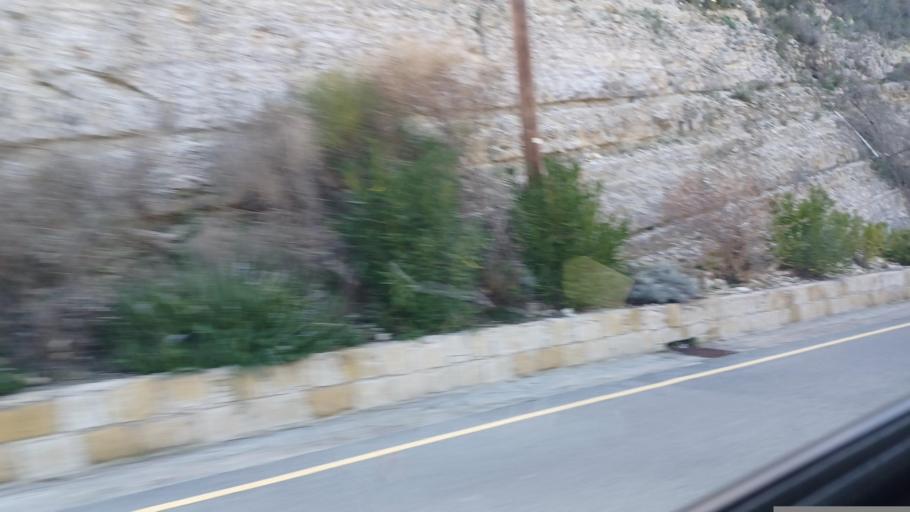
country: CY
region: Limassol
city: Pachna
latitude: 34.8362
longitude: 32.7931
